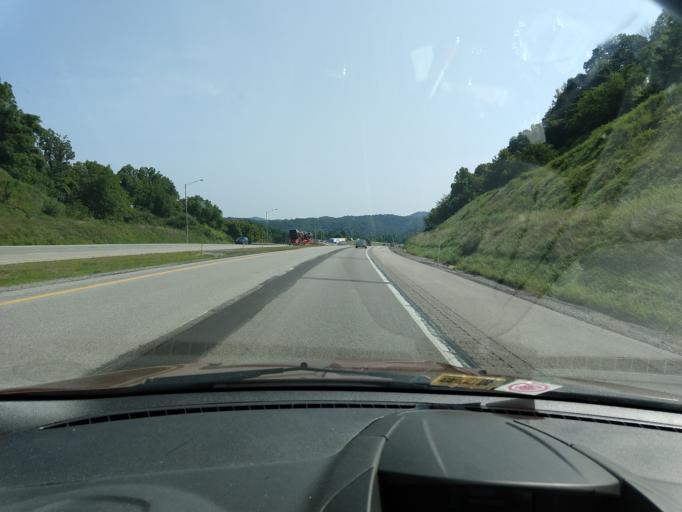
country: US
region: West Virginia
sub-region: Lewis County
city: Weston
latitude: 38.9096
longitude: -80.5998
